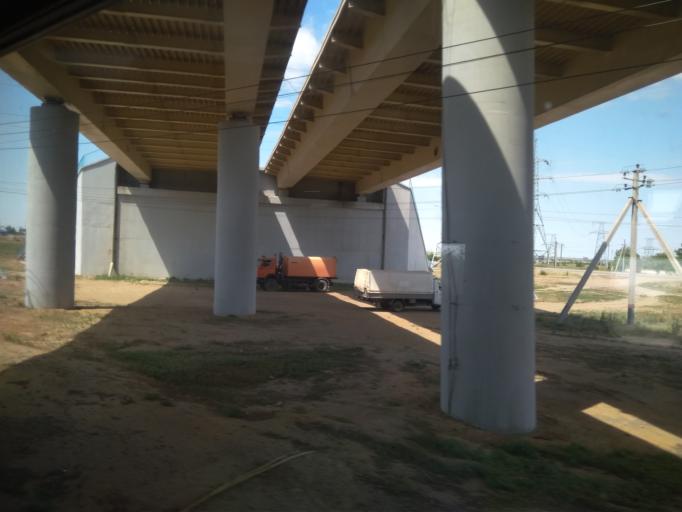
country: RU
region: Volgograd
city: Gumrak
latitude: 48.7612
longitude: 44.4195
